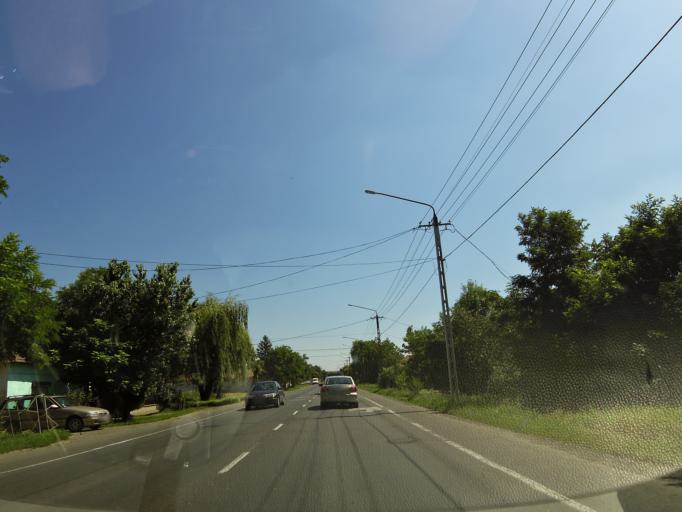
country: HU
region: Jasz-Nagykun-Szolnok
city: Fegyvernek
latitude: 47.2311
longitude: 20.5195
